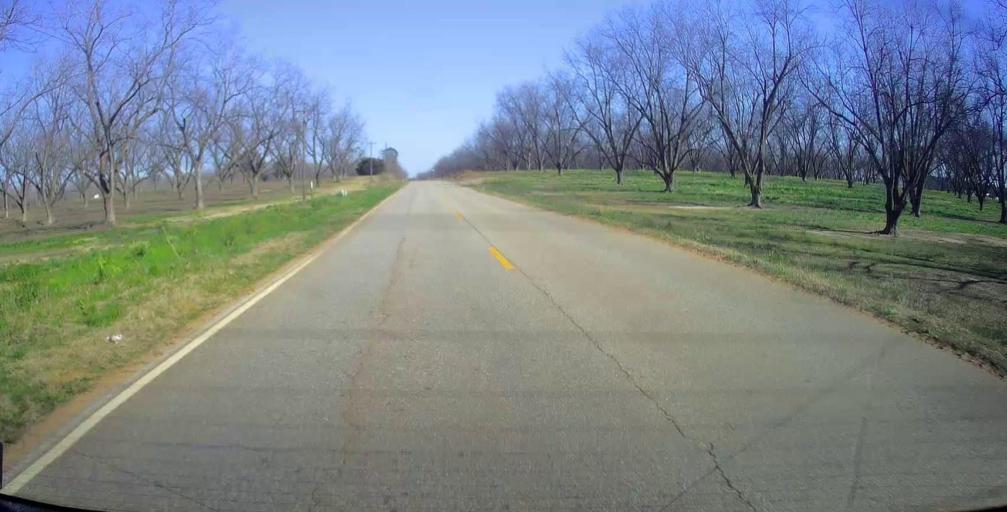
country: US
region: Georgia
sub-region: Peach County
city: Fort Valley
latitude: 32.6119
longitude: -83.9678
